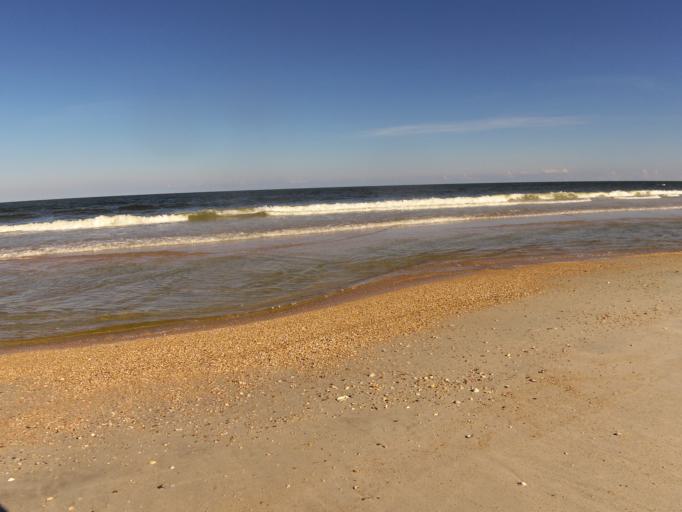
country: US
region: Florida
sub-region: Saint Johns County
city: Sawgrass
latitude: 30.1693
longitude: -81.3575
